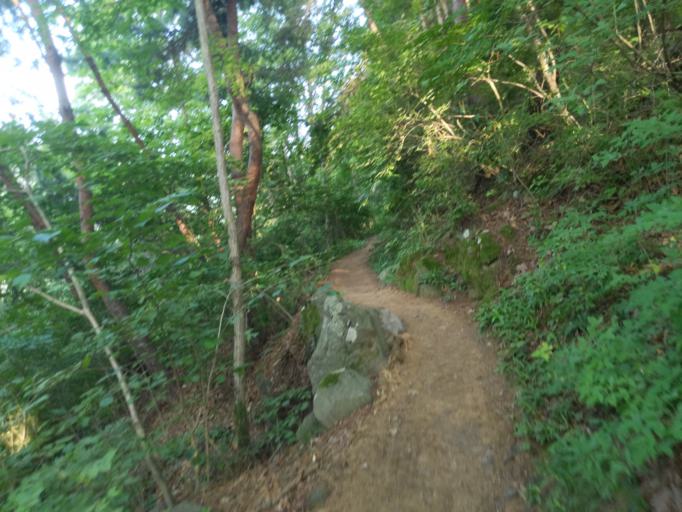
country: KR
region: Daegu
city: Hwawon
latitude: 35.7866
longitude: 128.5458
